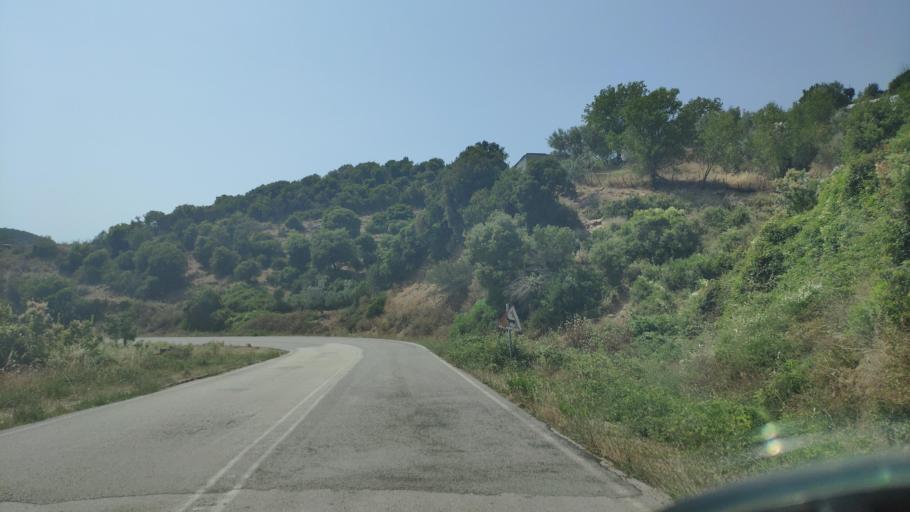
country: GR
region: Epirus
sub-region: Nomos Artas
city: Peta
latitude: 39.1758
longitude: 21.0770
